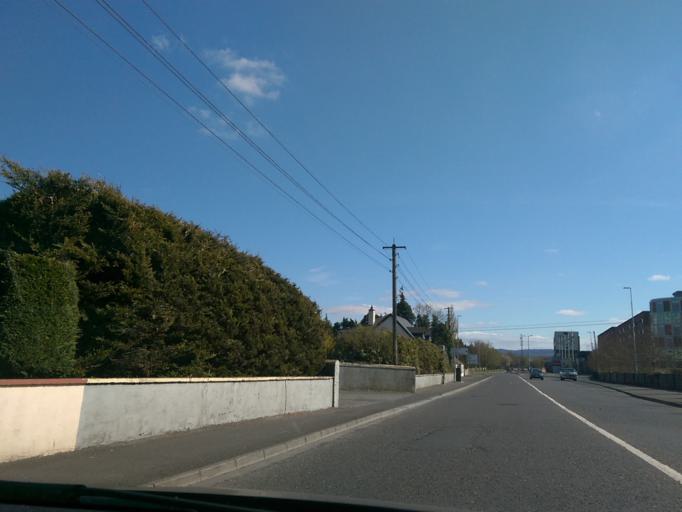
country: IE
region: Leinster
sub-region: Laois
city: Portlaoise
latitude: 53.0288
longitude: -7.3013
